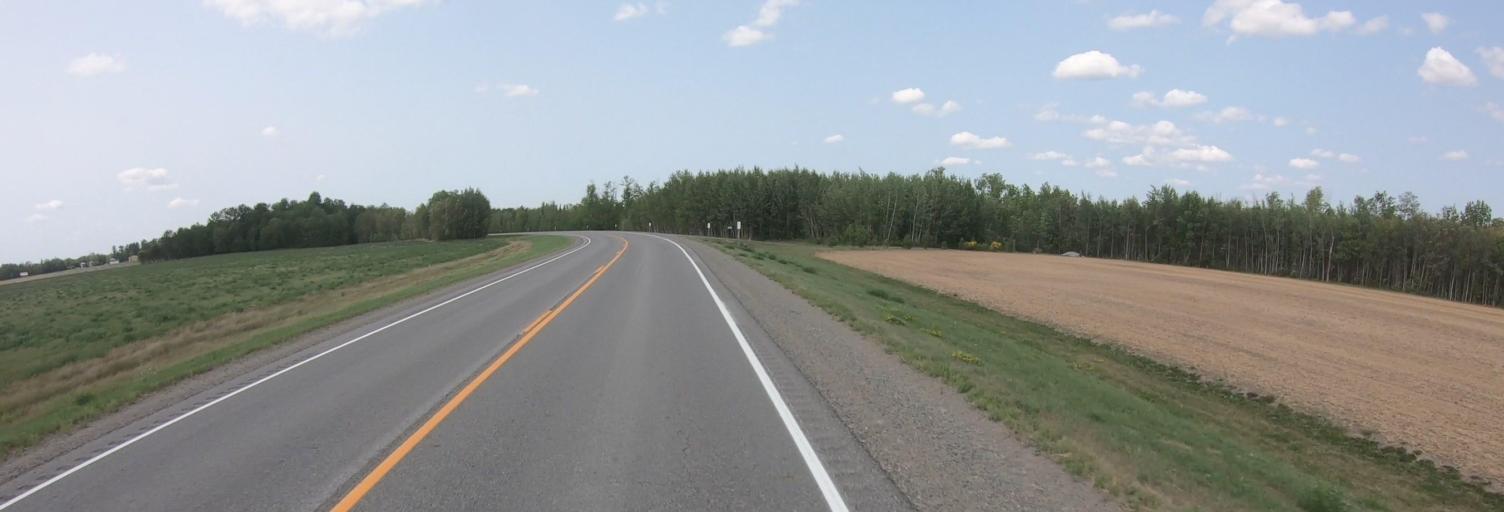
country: US
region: Minnesota
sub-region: Lake of the Woods County
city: Baudette
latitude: 48.6422
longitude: -94.1357
